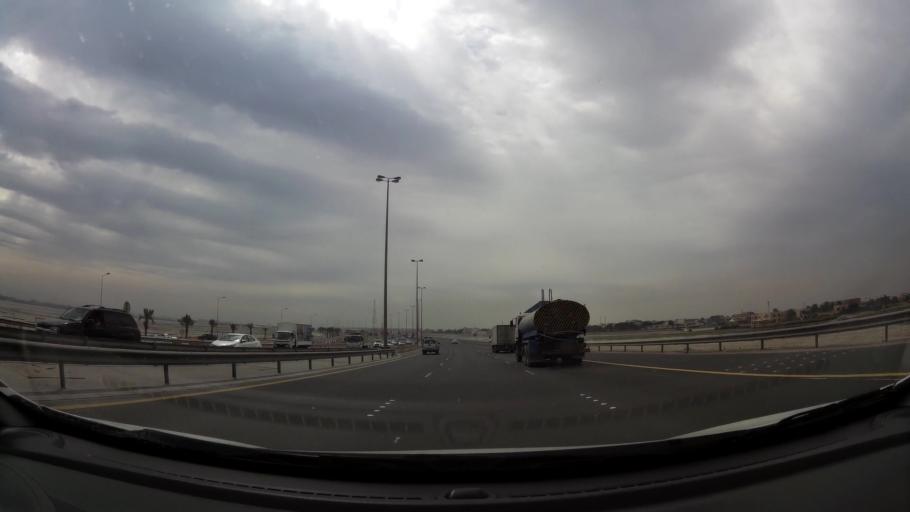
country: BH
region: Manama
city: Manama
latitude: 26.1925
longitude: 50.5886
